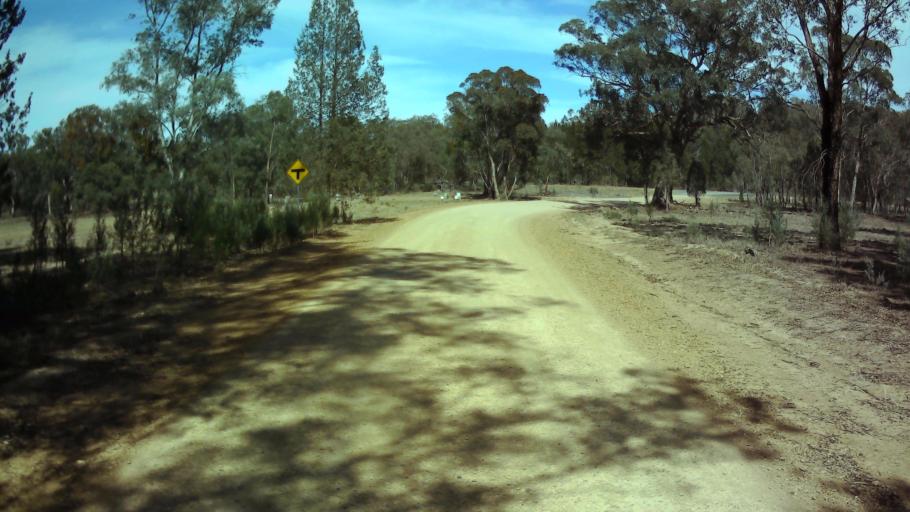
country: AU
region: New South Wales
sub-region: Weddin
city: Grenfell
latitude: -33.6852
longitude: 148.2767
